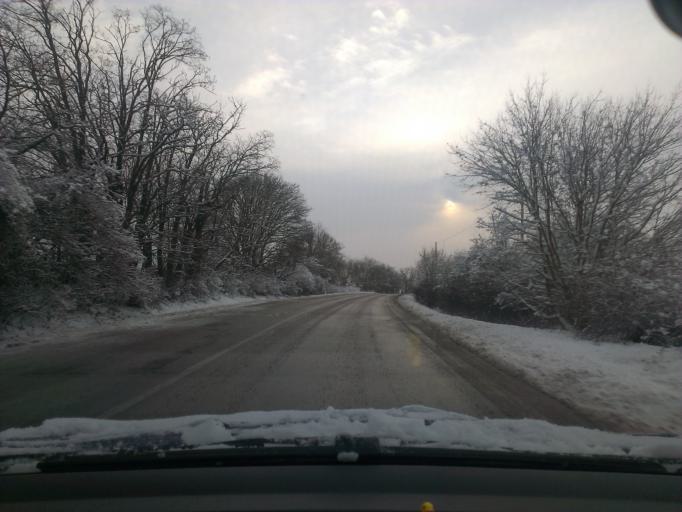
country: SK
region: Trnavsky
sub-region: Okres Trnava
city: Piestany
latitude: 48.5513
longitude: 17.9254
